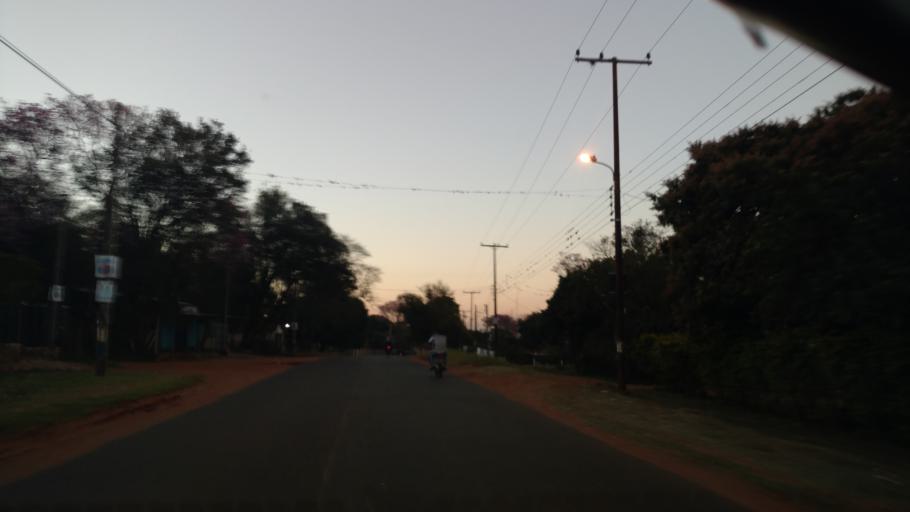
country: PY
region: Central
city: Guarambare
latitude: -25.4680
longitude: -57.4091
